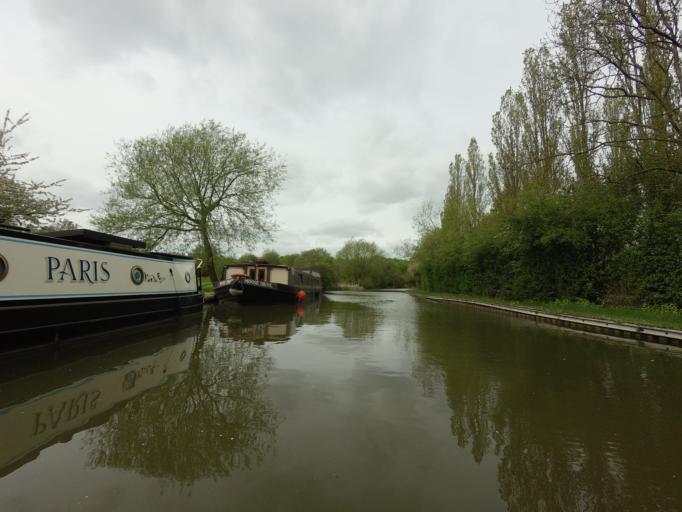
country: GB
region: England
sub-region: Milton Keynes
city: Milton Keynes
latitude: 52.0515
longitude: -0.7356
